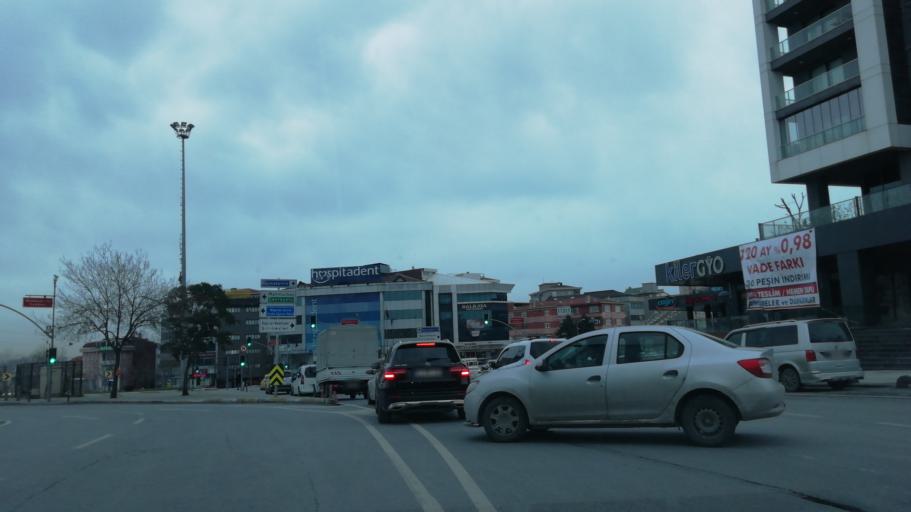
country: TR
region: Istanbul
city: Mahmutbey
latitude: 41.0454
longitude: 28.8293
